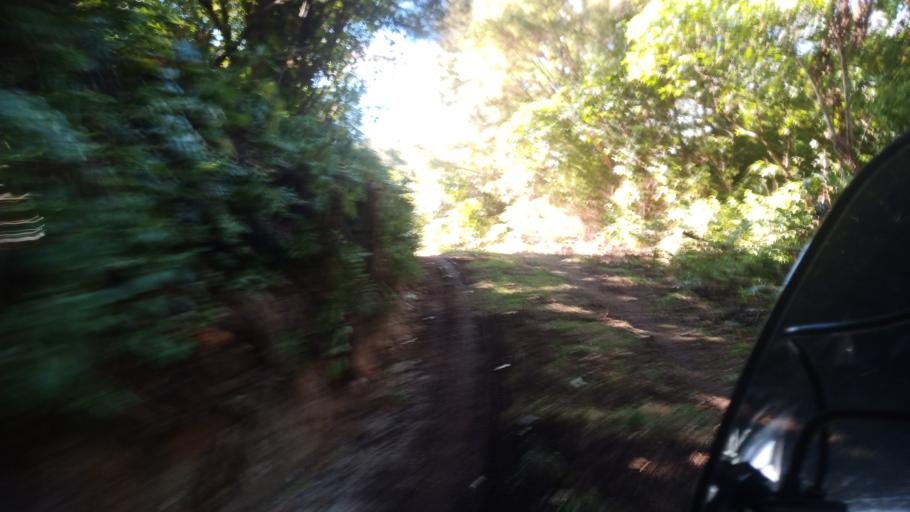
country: NZ
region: Hawke's Bay
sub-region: Wairoa District
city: Wairoa
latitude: -38.9981
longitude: 177.0681
